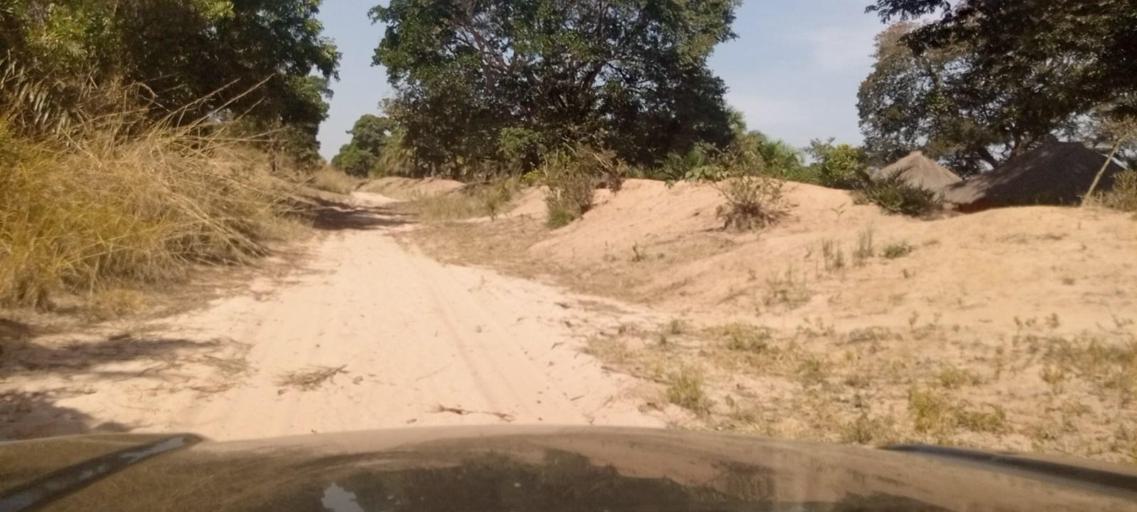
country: CD
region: Kasai-Oriental
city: Kabinda
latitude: -5.8041
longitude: 25.0180
